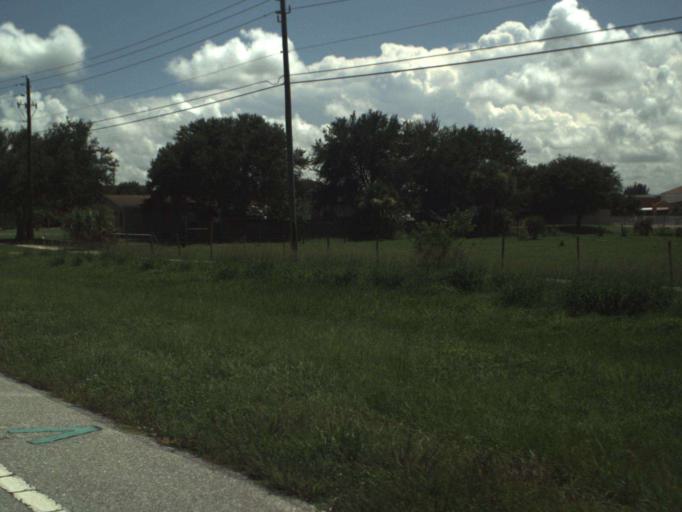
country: US
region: Florida
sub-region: Indian River County
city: Sebastian
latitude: 27.7605
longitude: -80.5112
